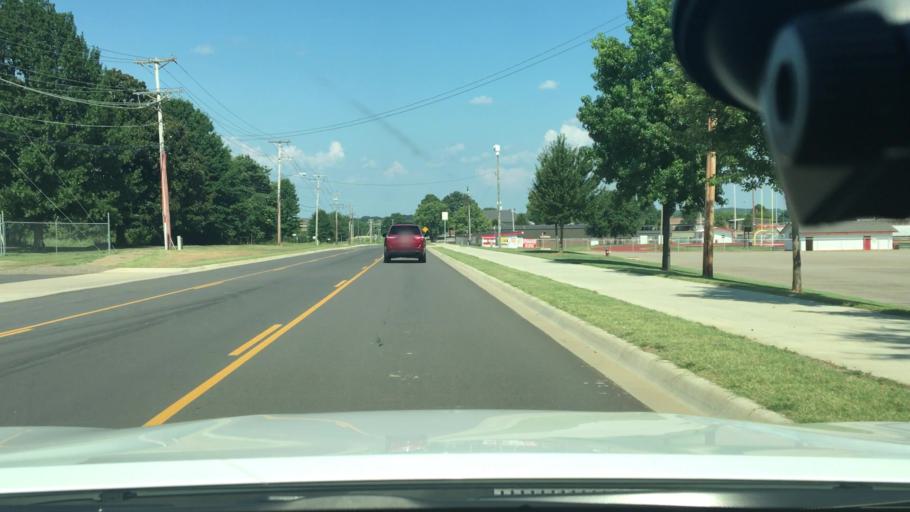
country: US
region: Arkansas
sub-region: Johnson County
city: Clarksville
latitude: 35.4618
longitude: -93.4889
